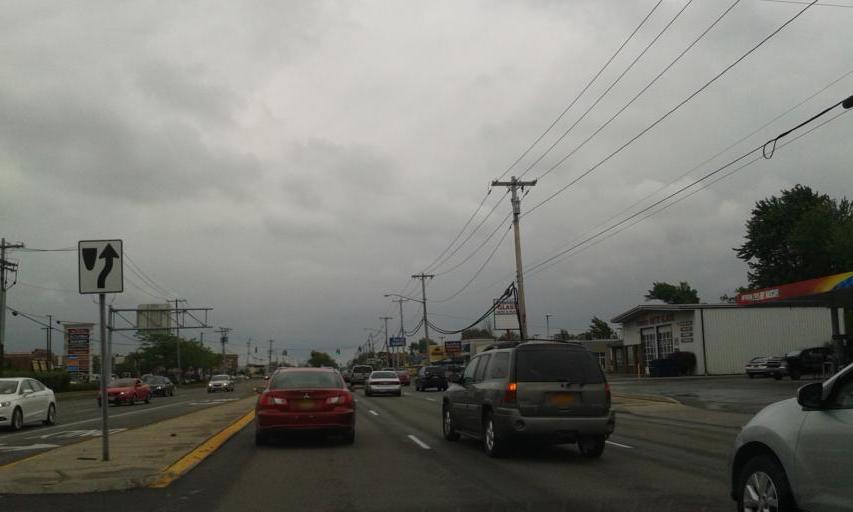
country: US
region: New York
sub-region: Erie County
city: Amherst
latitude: 43.0014
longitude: -78.8225
